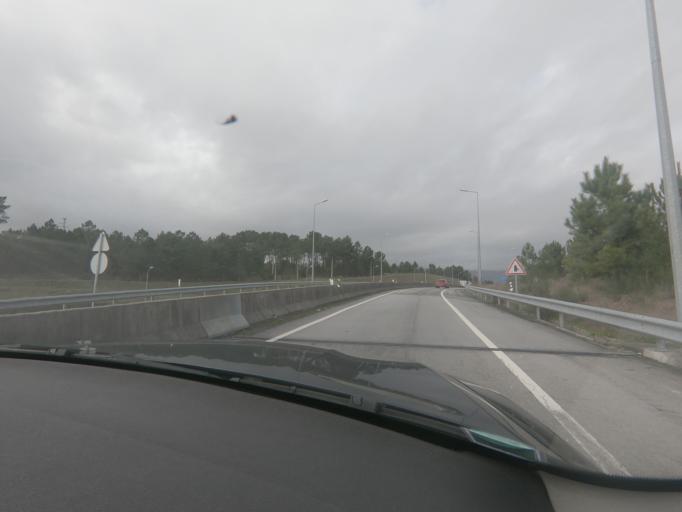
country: PT
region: Vila Real
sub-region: Vila Real
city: Vila Real
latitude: 41.3237
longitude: -7.7000
